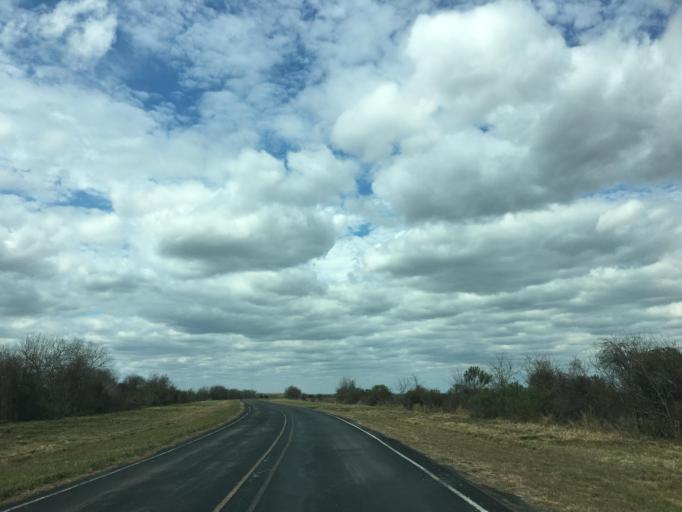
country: US
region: Texas
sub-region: Brazoria County
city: Oyster Creek
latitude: 29.0600
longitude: -95.2782
